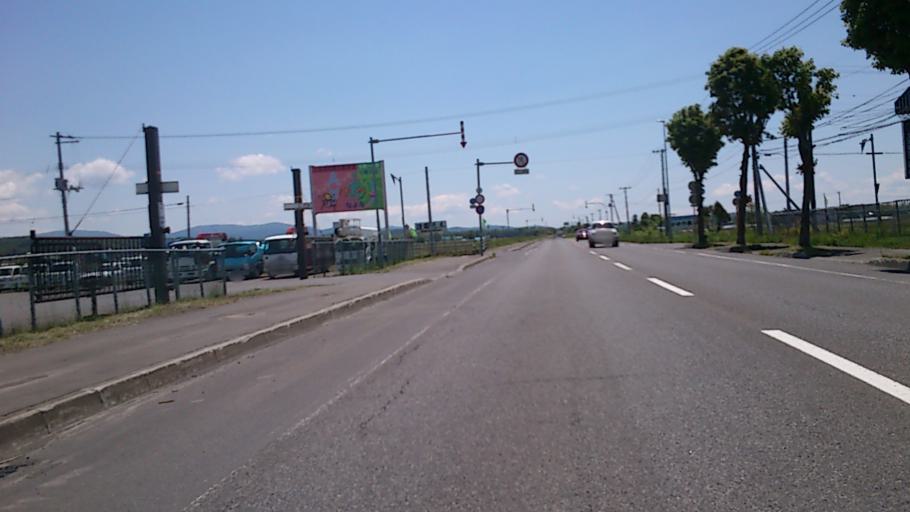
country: JP
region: Hokkaido
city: Nayoro
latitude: 44.3223
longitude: 142.4575
